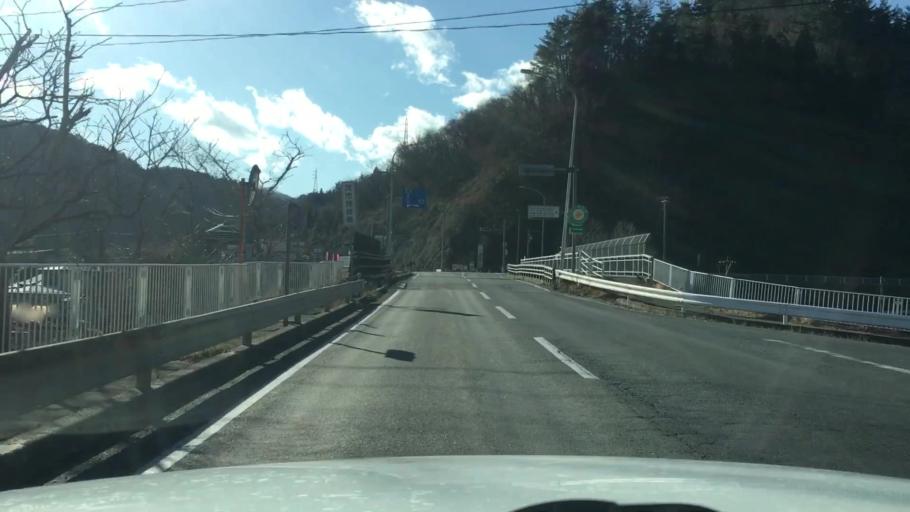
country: JP
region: Iwate
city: Miyako
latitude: 39.6199
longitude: 141.8019
